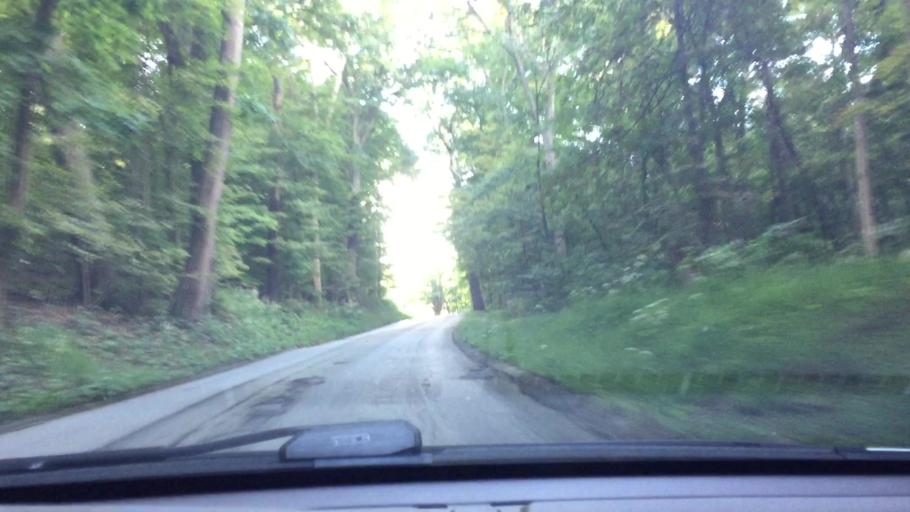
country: US
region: Pennsylvania
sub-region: Washington County
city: Thompsonville
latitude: 40.2683
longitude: -80.1434
